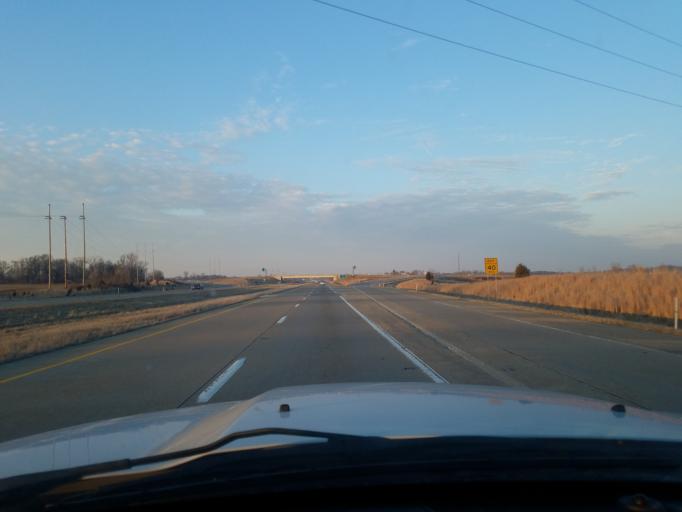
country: US
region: Indiana
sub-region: Vanderburgh County
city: Melody Hill
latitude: 38.0848
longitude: -87.4766
